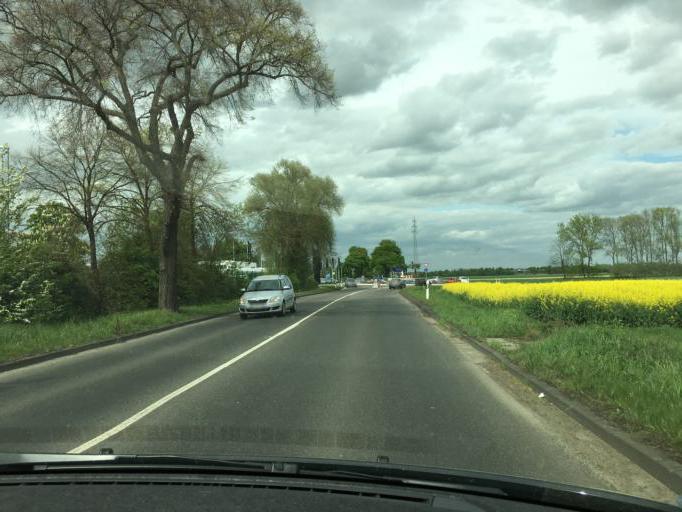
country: DE
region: North Rhine-Westphalia
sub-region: Regierungsbezirk Koln
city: Euskirchen
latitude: 50.6674
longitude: 6.8073
